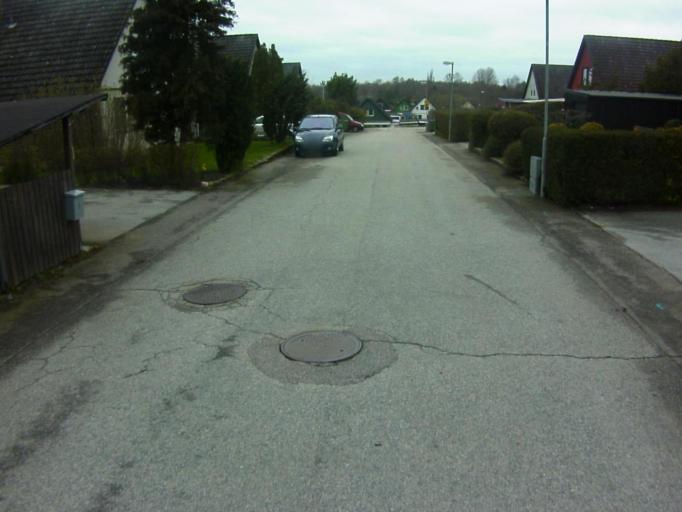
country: SE
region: Skane
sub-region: Kavlinge Kommun
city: Kaevlinge
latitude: 55.7693
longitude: 13.0861
